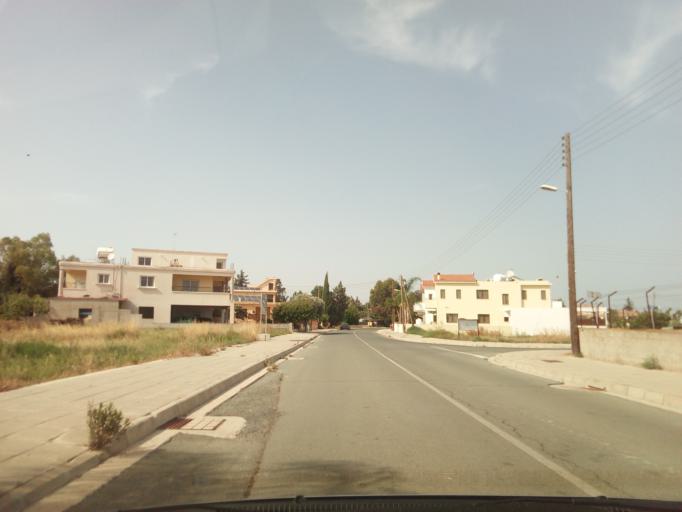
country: CY
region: Larnaka
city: Kiti
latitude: 34.8453
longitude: 33.5687
